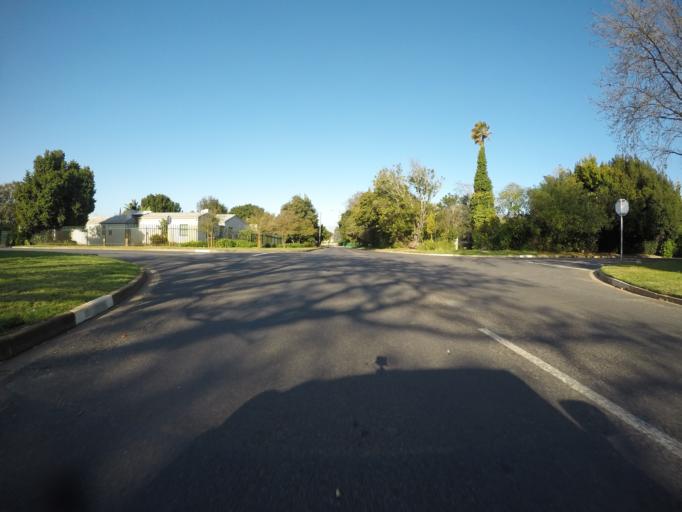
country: ZA
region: Western Cape
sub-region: City of Cape Town
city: Kraaifontein
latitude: -33.8437
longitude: 18.6573
